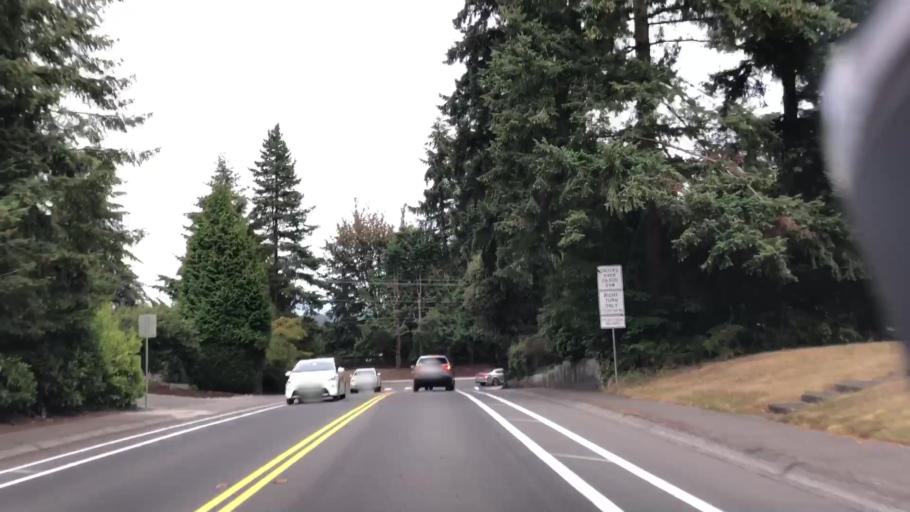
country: US
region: Washington
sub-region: King County
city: Kingsgate
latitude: 47.7304
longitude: -122.1650
